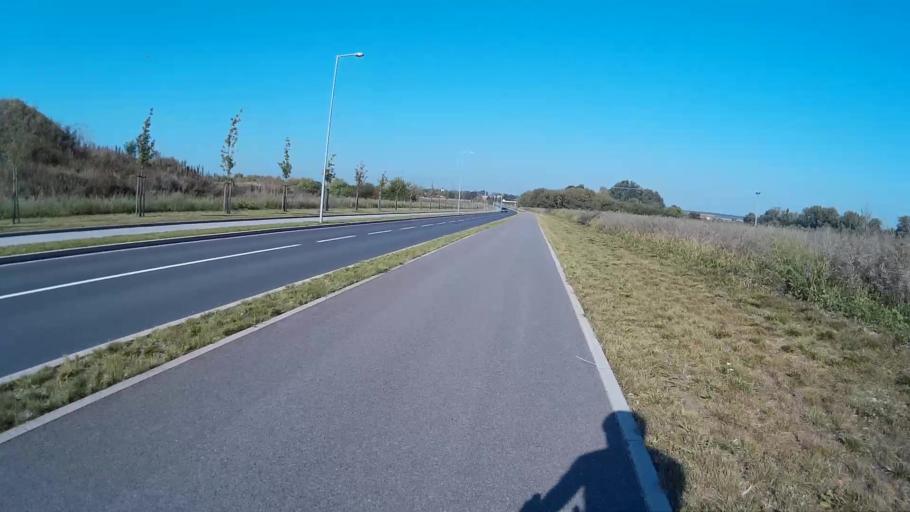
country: CZ
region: South Moravian
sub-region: Okres Breclav
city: Dolni Dunajovice
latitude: 48.9005
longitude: 16.5580
